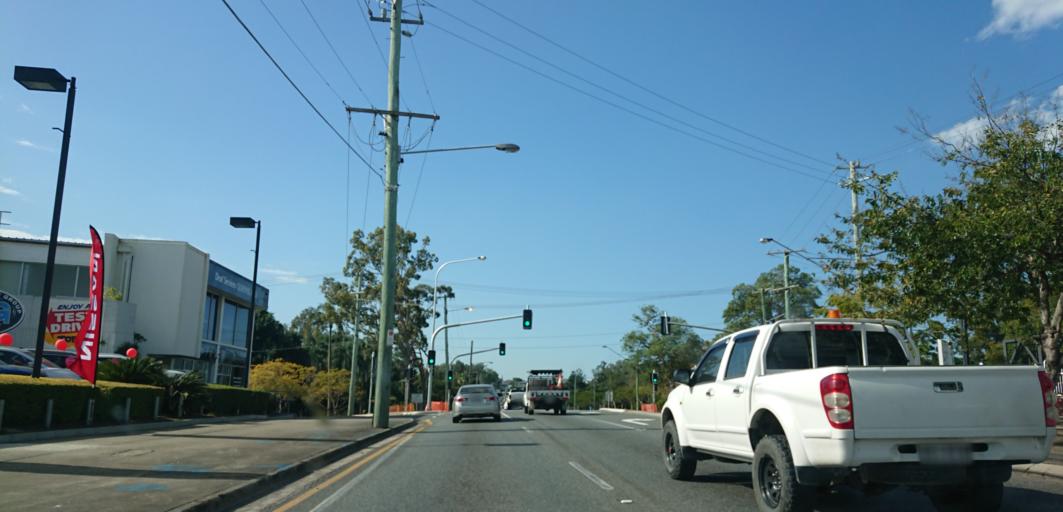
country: AU
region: Queensland
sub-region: Brisbane
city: Yeerongpilly
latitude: -27.5273
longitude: 153.0207
